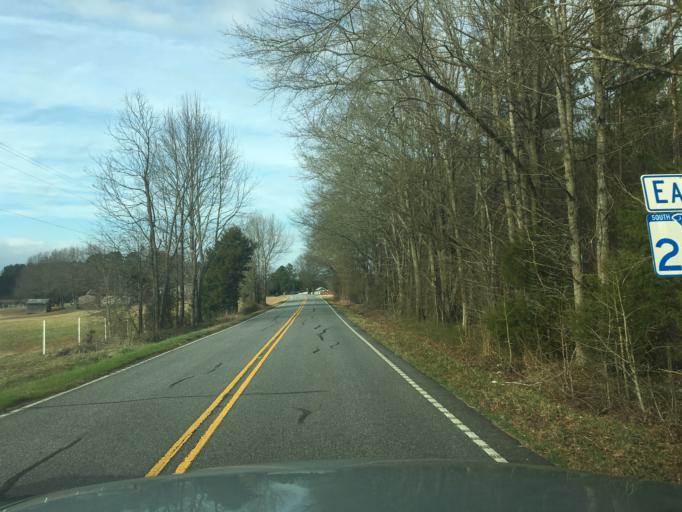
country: US
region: South Carolina
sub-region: Abbeville County
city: Lake Secession
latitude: 34.3636
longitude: -82.5203
